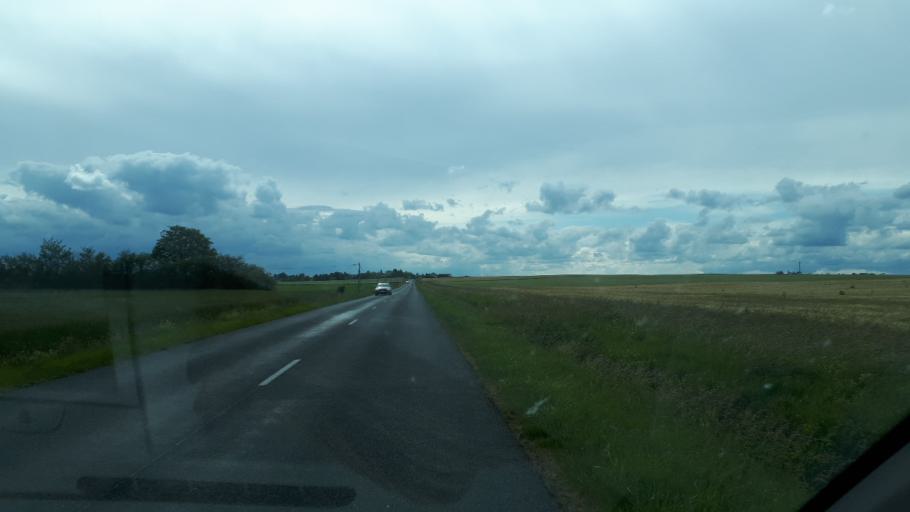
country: FR
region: Centre
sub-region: Departement du Cher
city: Mehun-sur-Yevre
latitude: 47.0814
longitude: 2.2190
